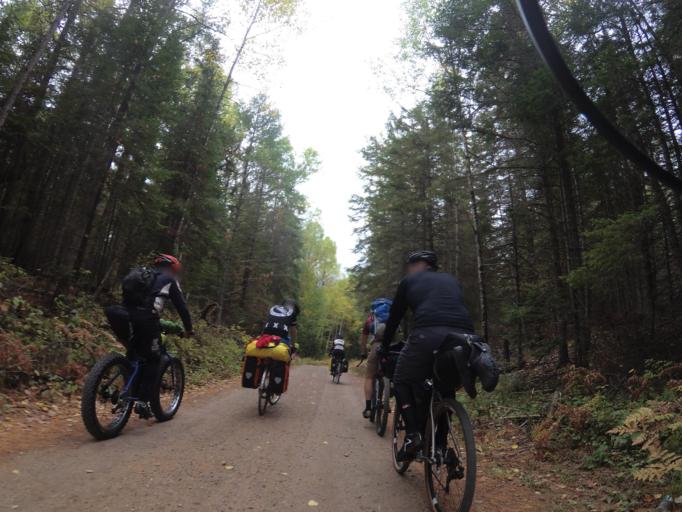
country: CA
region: Ontario
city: Pembroke
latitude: 45.2881
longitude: -77.2452
